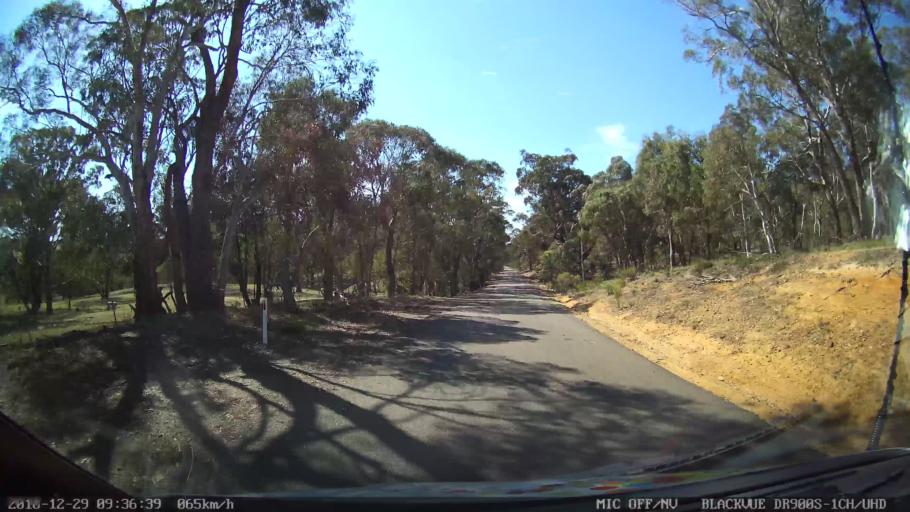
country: AU
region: New South Wales
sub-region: Upper Lachlan Shire
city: Crookwell
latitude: -34.6343
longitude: 149.3666
